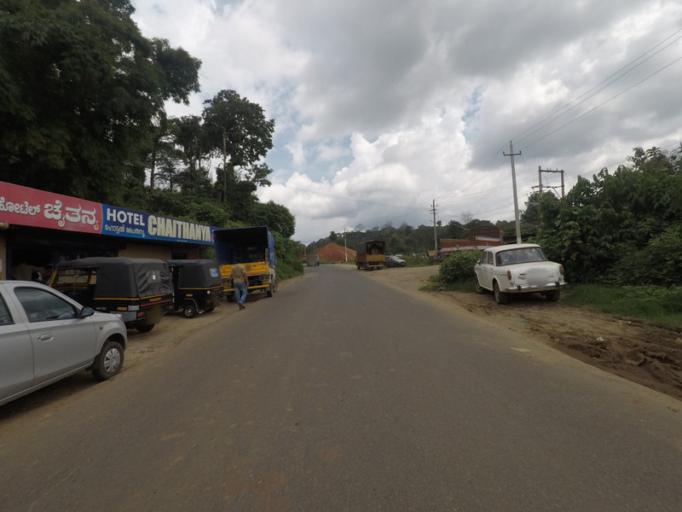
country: IN
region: Karnataka
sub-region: Kodagu
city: Virarajendrapet
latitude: 12.3035
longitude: 75.8700
